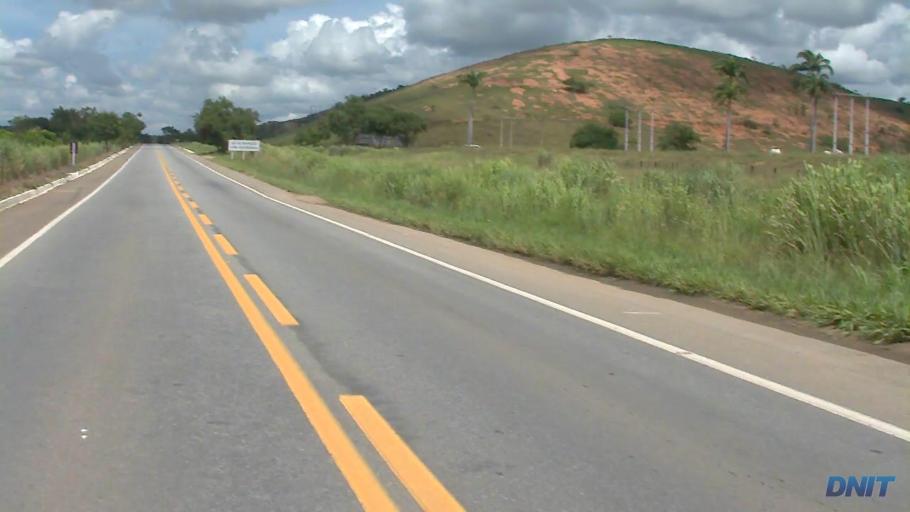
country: BR
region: Minas Gerais
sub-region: Governador Valadares
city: Governador Valadares
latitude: -18.9432
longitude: -42.0622
